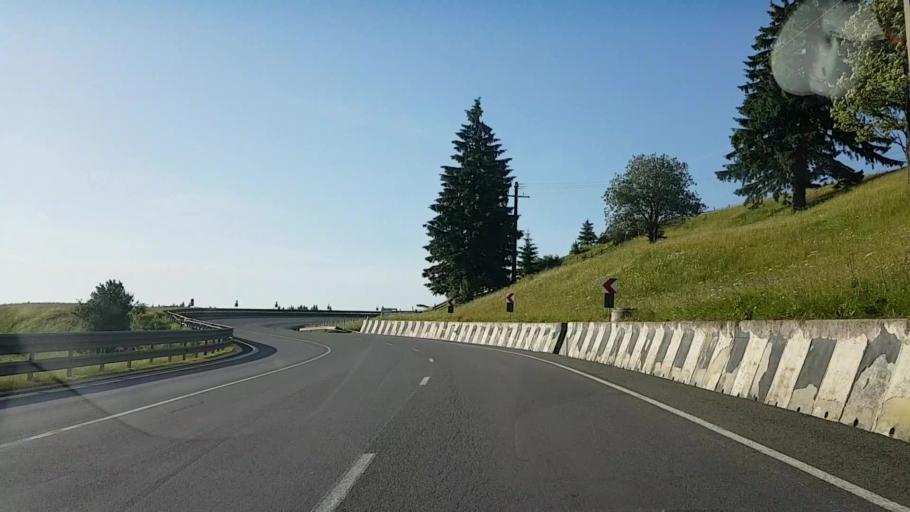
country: RO
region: Bistrita-Nasaud
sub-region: Comuna Lunca Ilvei
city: Lunca Ilvei
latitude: 47.2465
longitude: 25.0210
